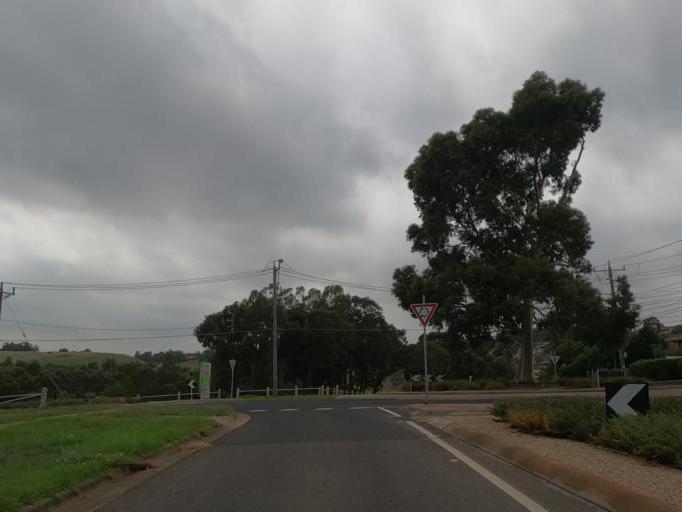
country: AU
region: Victoria
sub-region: Hume
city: Broadmeadows
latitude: -37.6769
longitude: 144.9098
